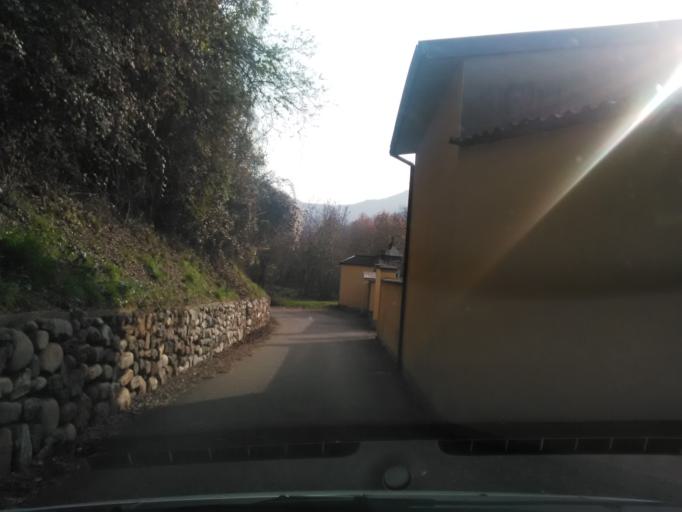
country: IT
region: Piedmont
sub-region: Provincia di Vercelli
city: Guardabosone
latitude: 45.6987
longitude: 8.2547
